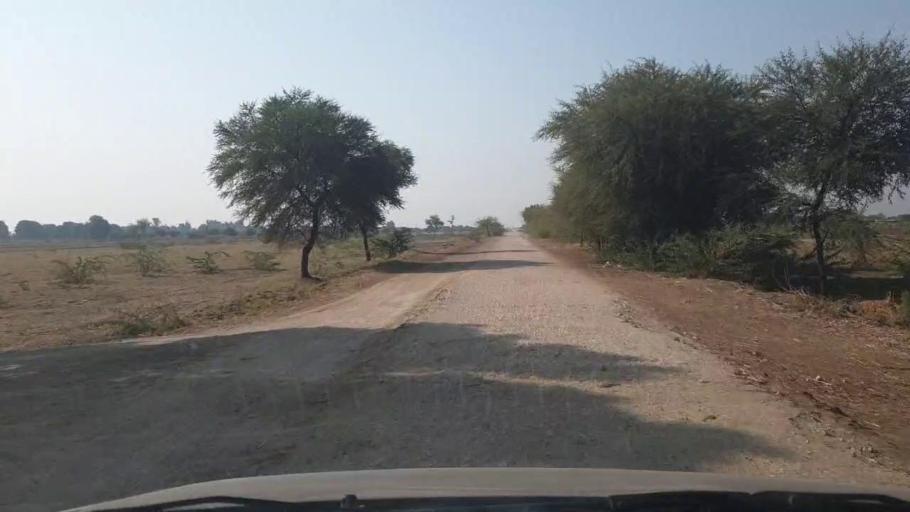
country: PK
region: Sindh
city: Mirwah Gorchani
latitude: 25.2753
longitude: 69.1203
